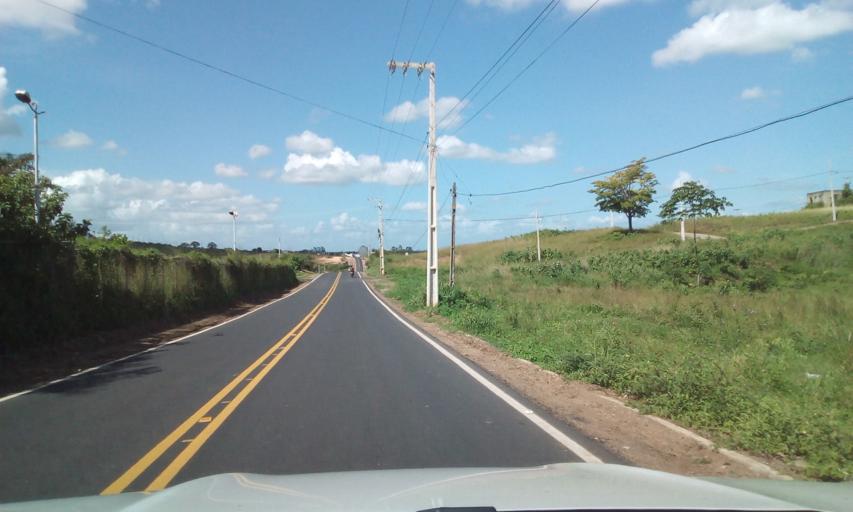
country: BR
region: Paraiba
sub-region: Guarabira
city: Guarabira
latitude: -6.8537
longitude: -35.4784
